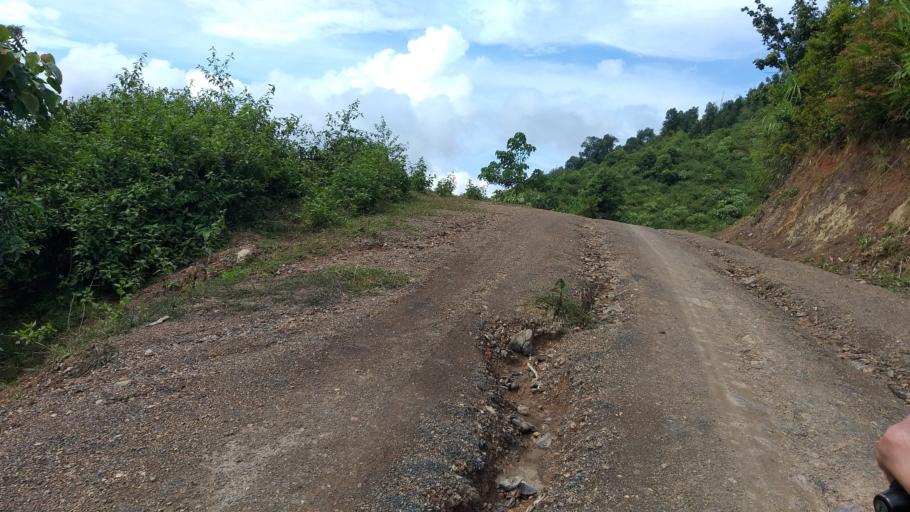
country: VN
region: Huyen Dien Bien
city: Dien Bien Phu
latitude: 21.4718
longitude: 102.6802
